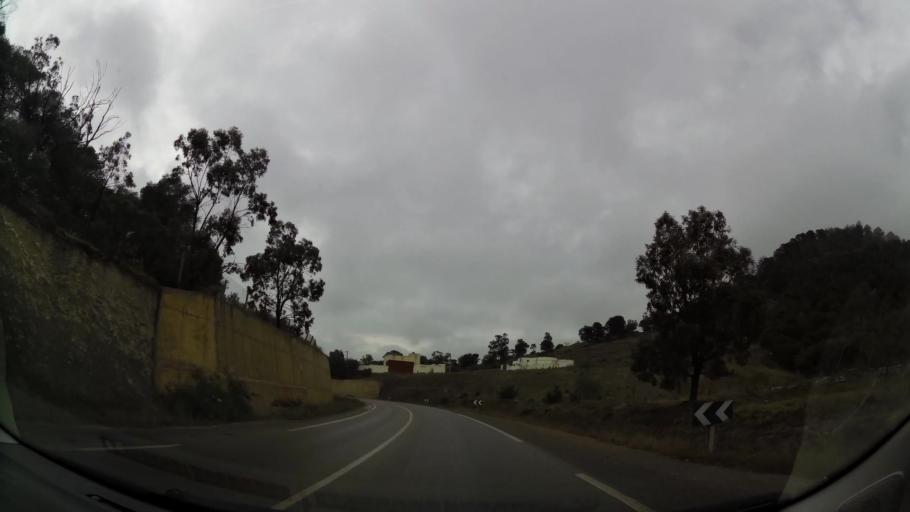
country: MA
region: Oriental
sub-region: Nador
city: Nador
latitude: 35.1523
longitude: -3.0203
